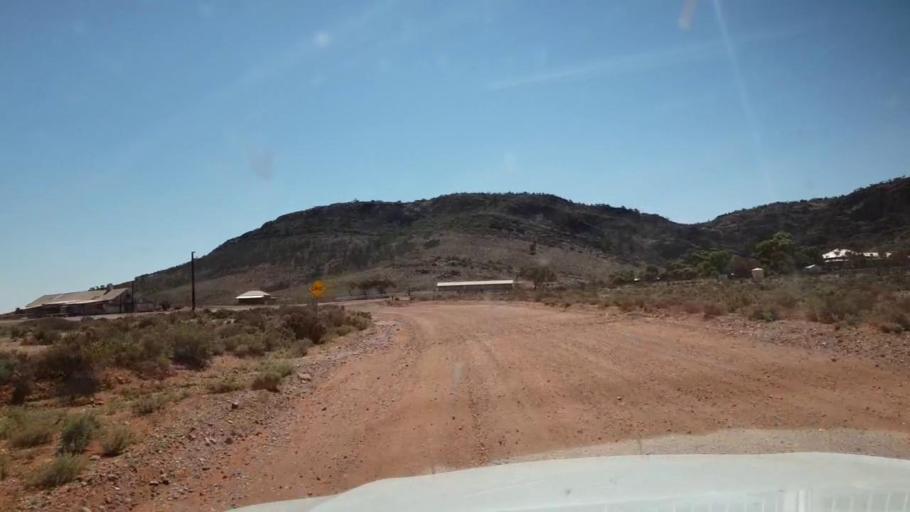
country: AU
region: South Australia
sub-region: Whyalla
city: Whyalla
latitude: -32.6864
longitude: 137.1260
